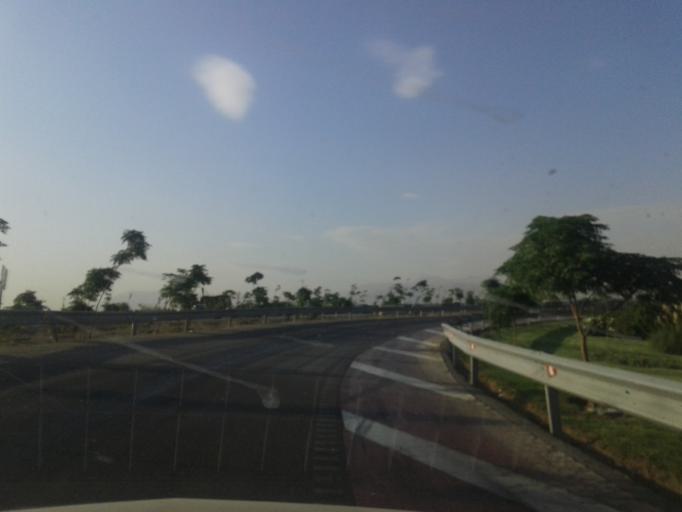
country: IR
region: Tehran
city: Eslamshahr
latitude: 35.6486
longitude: 51.2733
